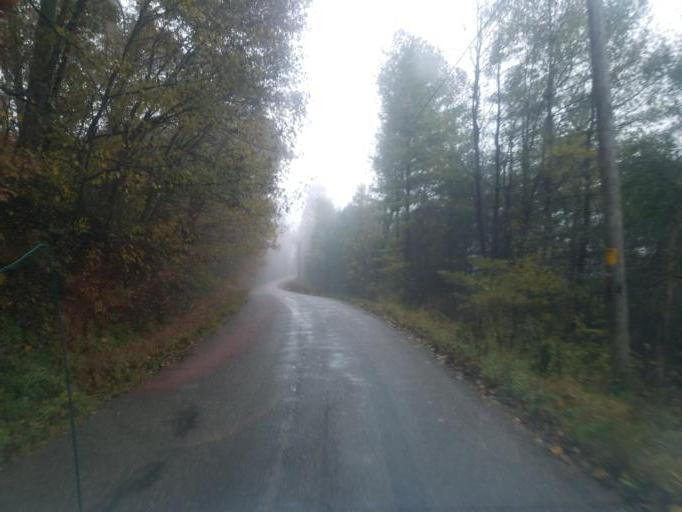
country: US
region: Ohio
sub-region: Athens County
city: Glouster
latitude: 39.4787
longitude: -81.9499
